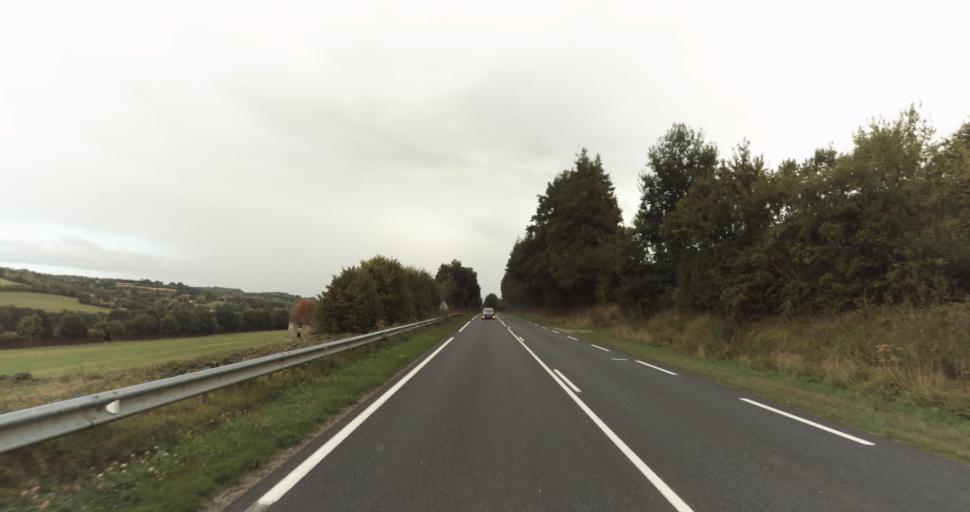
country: FR
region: Lower Normandy
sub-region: Departement de l'Orne
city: Gace
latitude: 48.8394
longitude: 0.2700
